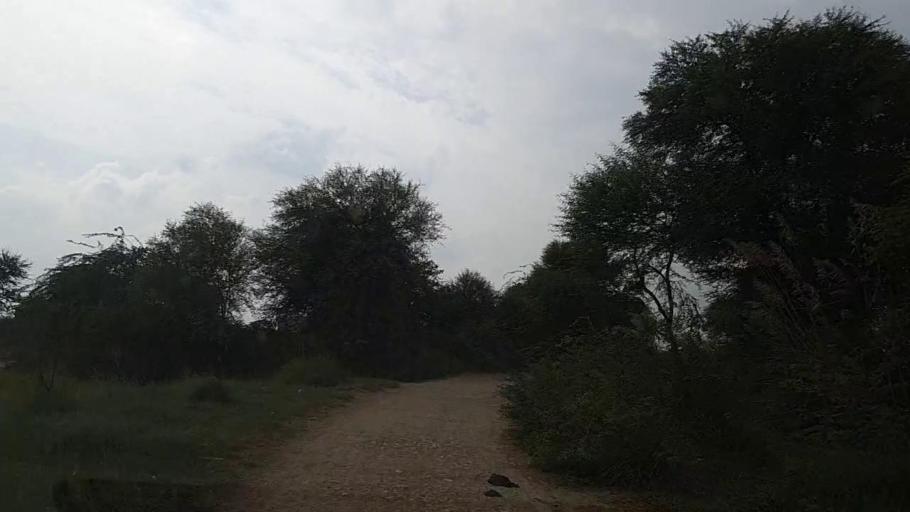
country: PK
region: Sindh
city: Mirpur Batoro
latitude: 24.5906
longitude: 68.1267
